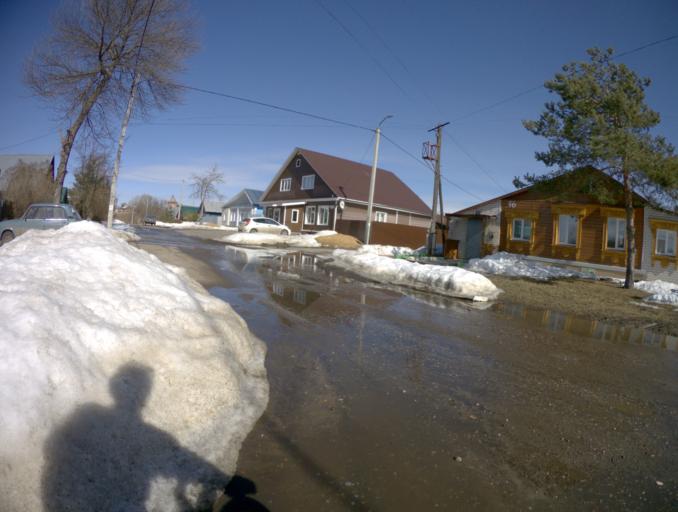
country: RU
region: Vladimir
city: Suzdal'
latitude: 56.4310
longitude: 40.4340
